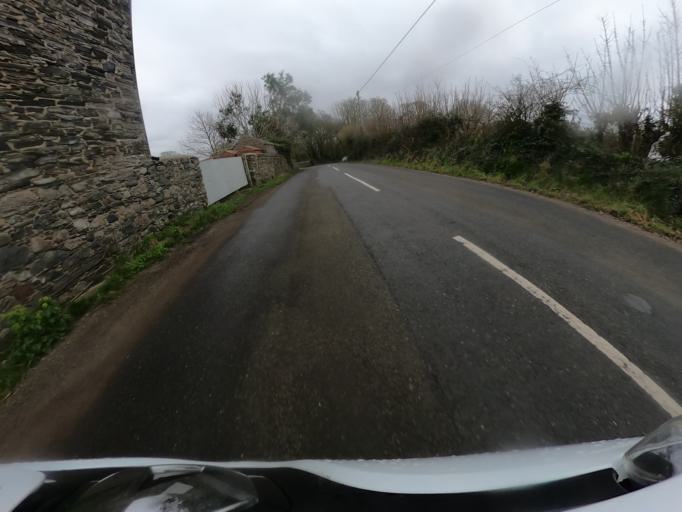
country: IM
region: Ramsey
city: Ramsey
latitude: 54.3500
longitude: -4.5054
